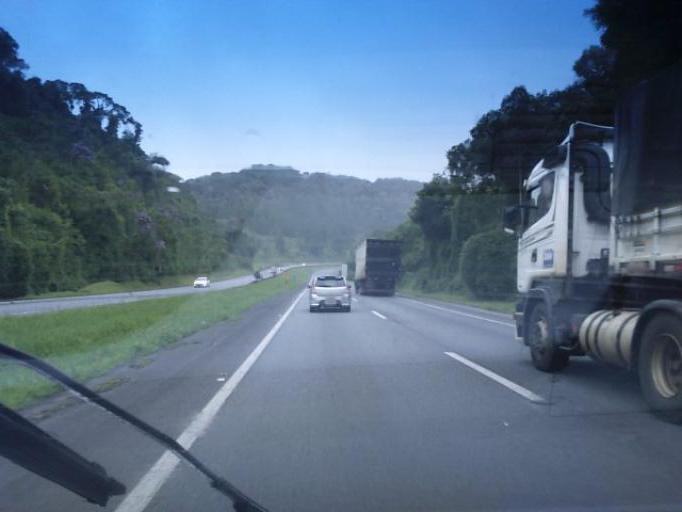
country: BR
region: Parana
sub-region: Antonina
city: Antonina
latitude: -25.0825
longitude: -48.6163
